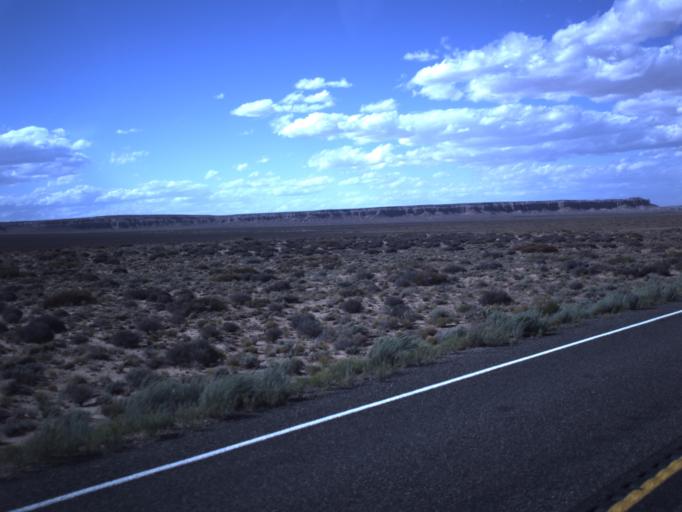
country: US
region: Utah
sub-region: Wayne County
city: Loa
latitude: 38.1687
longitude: -110.6236
